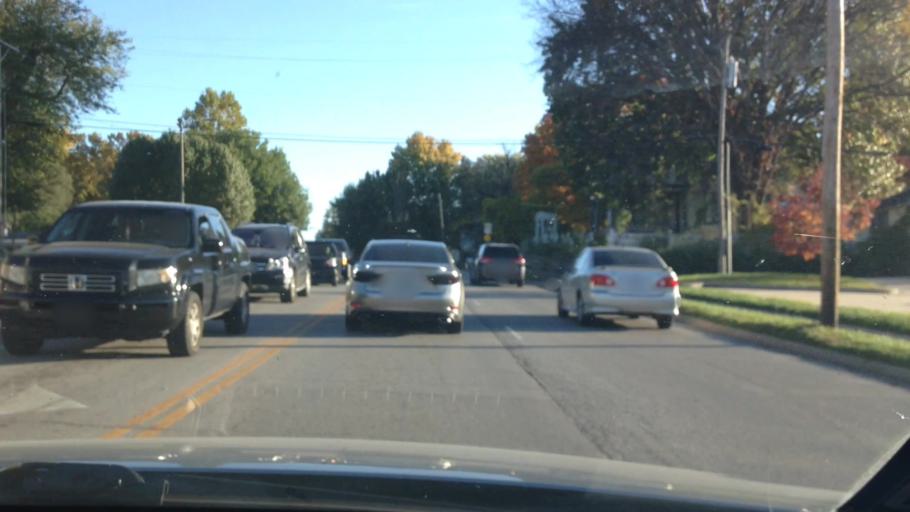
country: US
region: Kansas
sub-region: Leavenworth County
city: Leavenworth
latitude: 39.3108
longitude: -94.9122
